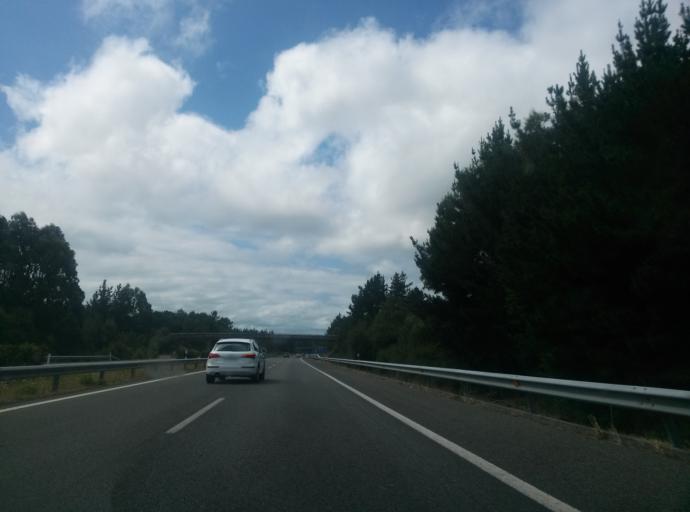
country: ES
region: Galicia
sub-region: Provincia de Lugo
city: Outeiro de Rei
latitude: 43.0965
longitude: -7.5941
